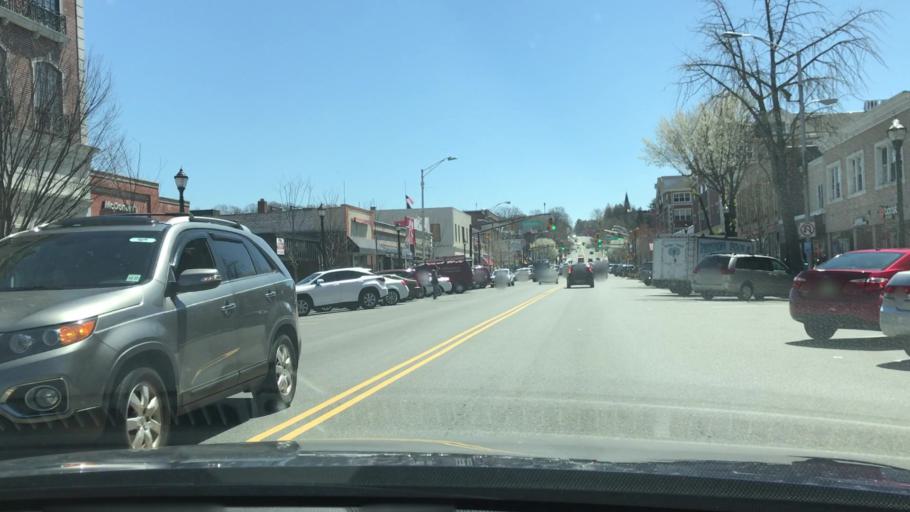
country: US
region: New Jersey
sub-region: Bergen County
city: Englewood
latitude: 40.8953
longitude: -73.9773
